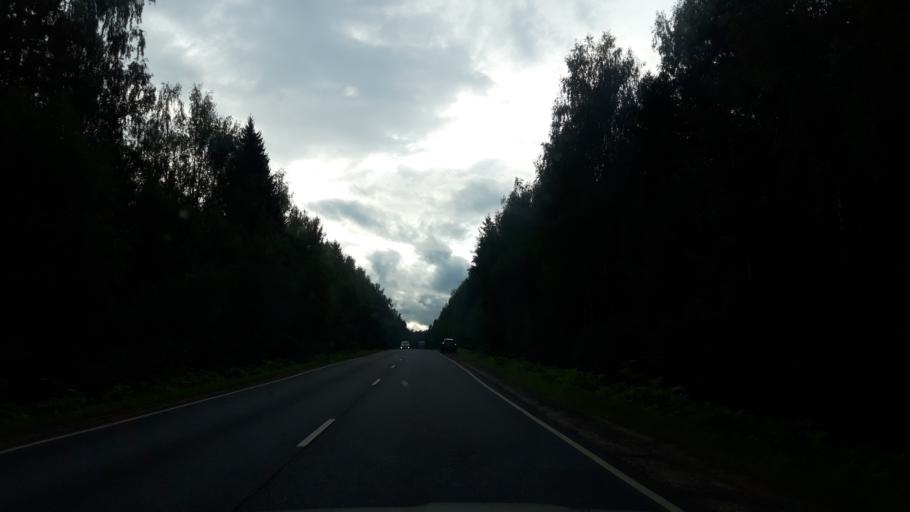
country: RU
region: Moskovskaya
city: Solnechnogorsk
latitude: 56.0942
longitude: 36.8914
